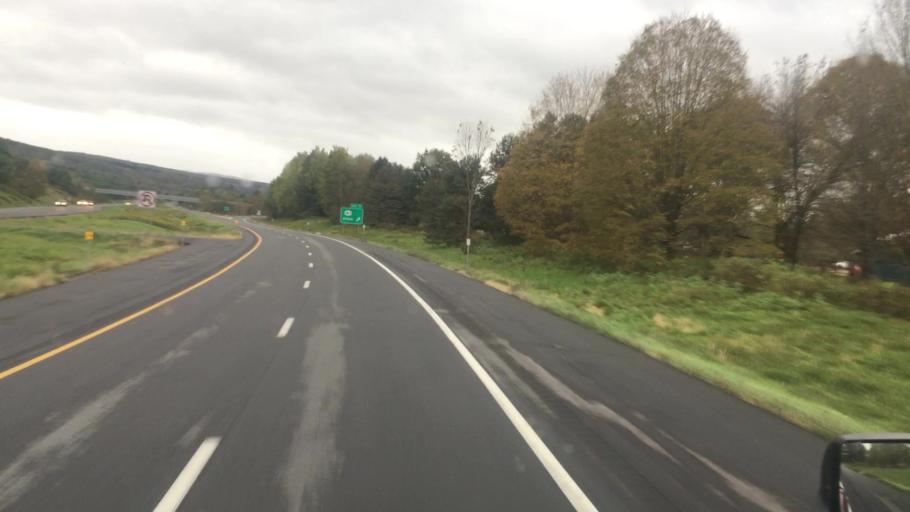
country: US
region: New York
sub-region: Chenango County
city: Bainbridge
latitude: 42.2290
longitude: -75.5110
